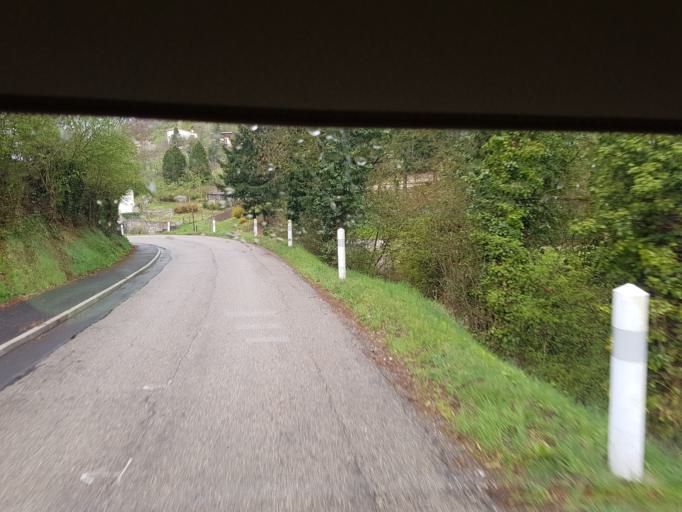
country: FR
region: Rhone-Alpes
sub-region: Departement de la Loire
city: Le Chambon-Feugerolles
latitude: 45.4005
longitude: 4.3223
